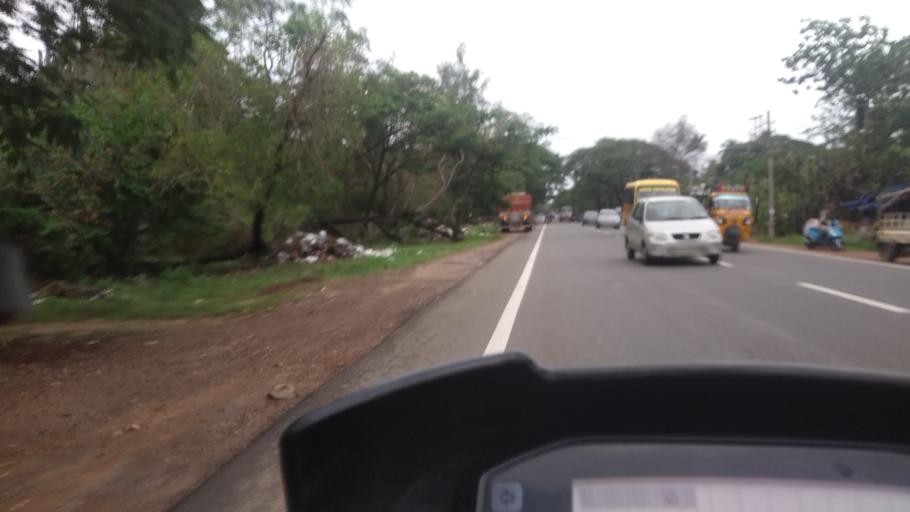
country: IN
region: Kerala
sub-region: Alappuzha
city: Alleppey
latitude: 9.5501
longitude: 76.3274
